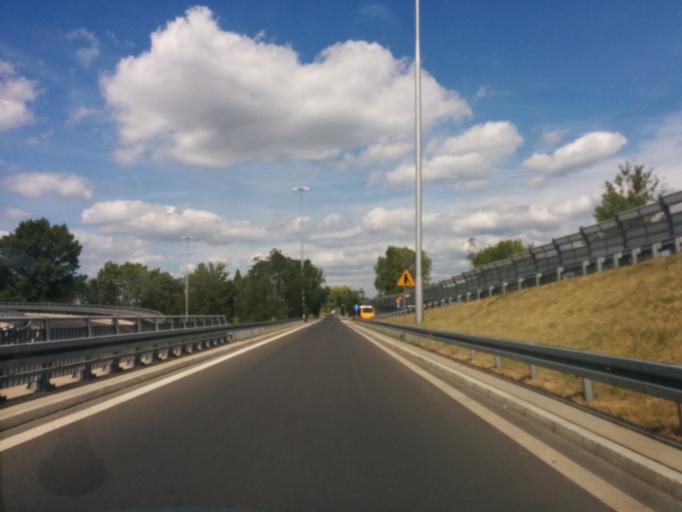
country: PL
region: Masovian Voivodeship
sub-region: Warszawa
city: Targowek
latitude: 52.2956
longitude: 21.0159
